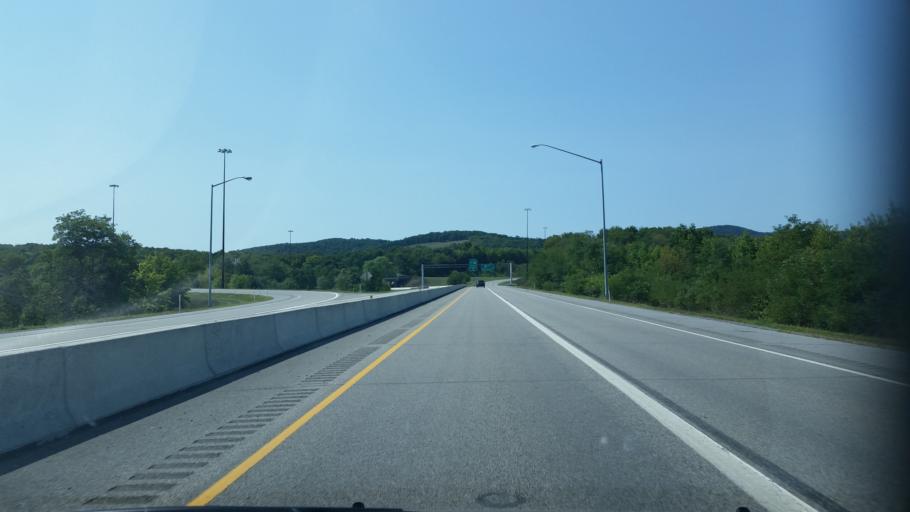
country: US
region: Pennsylvania
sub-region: Blair County
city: Duncansville
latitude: 40.4449
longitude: -78.4396
